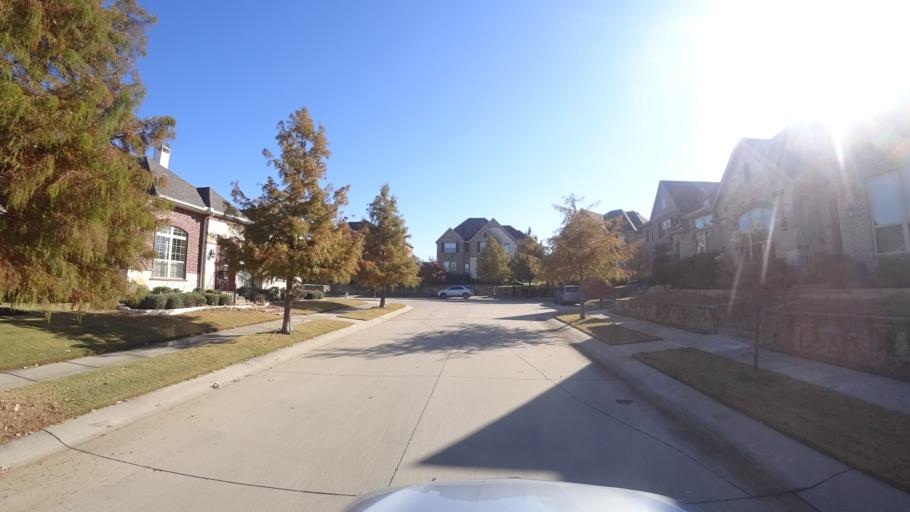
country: US
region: Texas
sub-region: Denton County
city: The Colony
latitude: 33.0380
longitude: -96.9196
